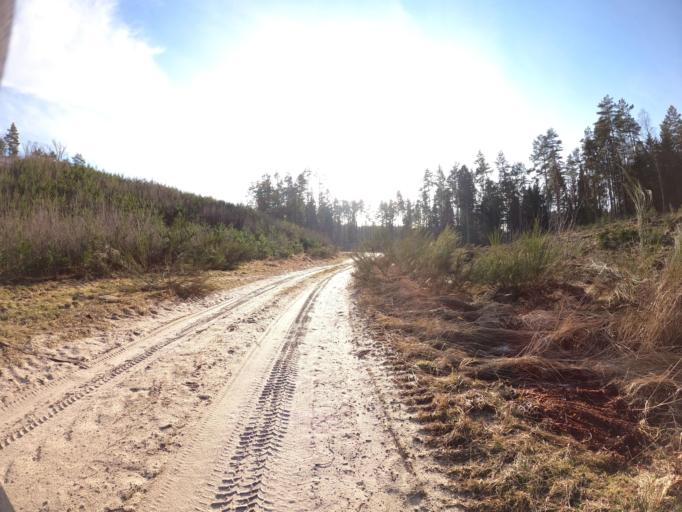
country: PL
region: West Pomeranian Voivodeship
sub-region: Powiat koszalinski
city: Polanow
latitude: 54.2158
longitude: 16.6431
